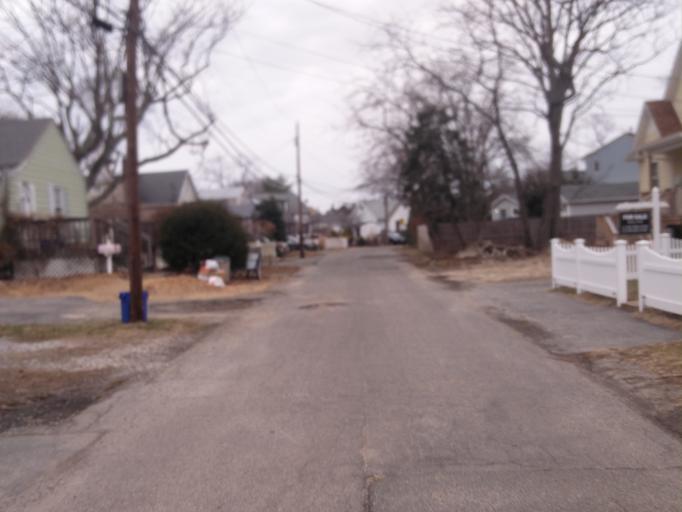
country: US
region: New York
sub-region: Nassau County
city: Bayville
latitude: 40.9064
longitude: -73.5445
